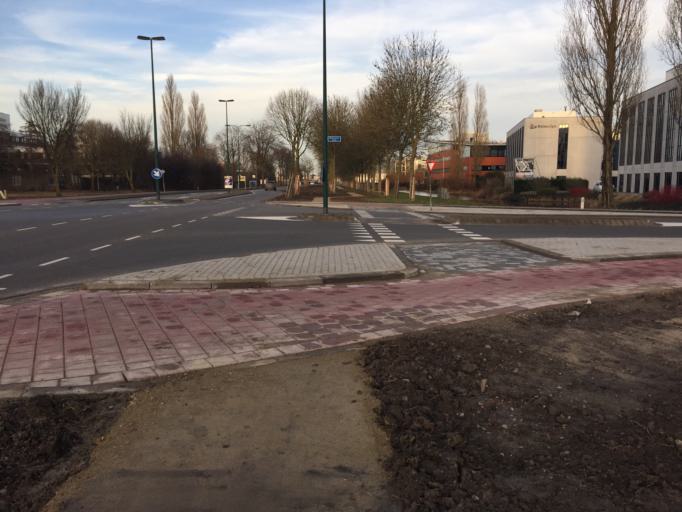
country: NL
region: Utrecht
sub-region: Gemeente Woerden
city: Woerden
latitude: 52.0775
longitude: 4.8902
